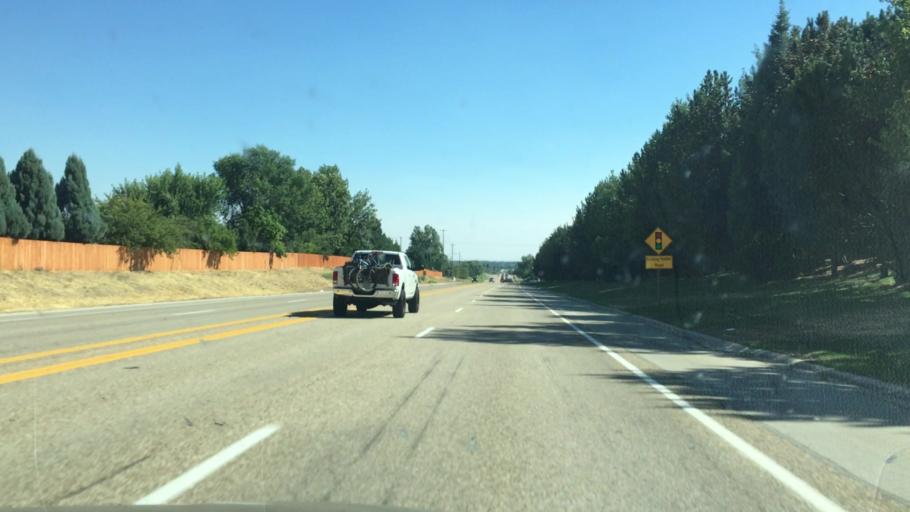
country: US
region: Idaho
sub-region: Ada County
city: Eagle
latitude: 43.7099
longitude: -116.3189
